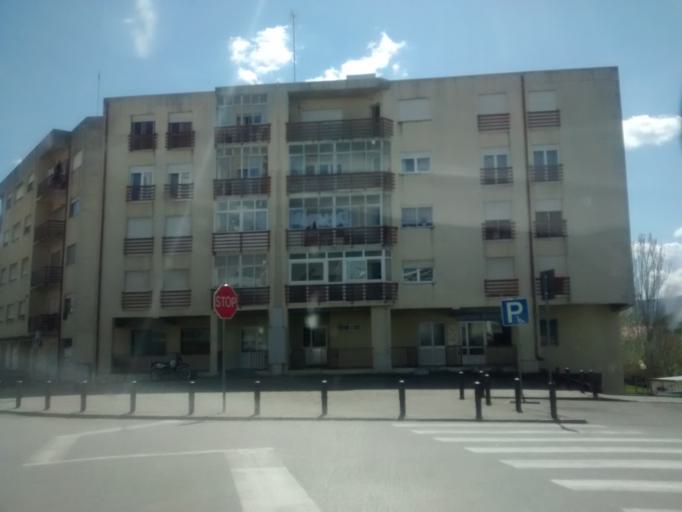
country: PT
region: Braganca
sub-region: Braganca Municipality
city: Braganca
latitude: 41.8023
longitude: -6.7731
